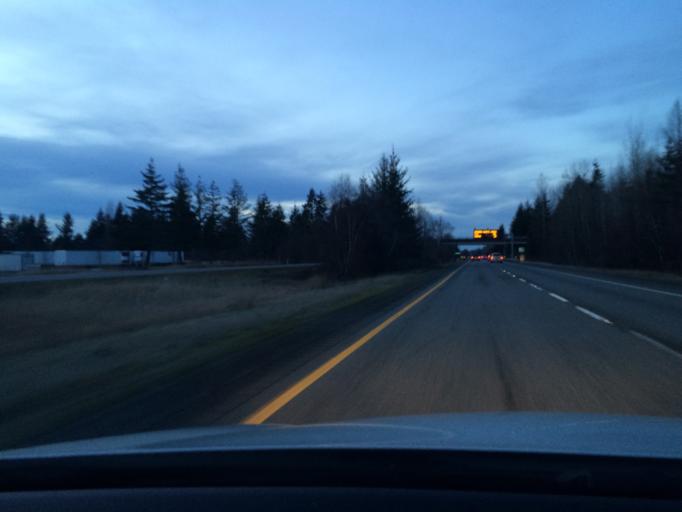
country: US
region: Washington
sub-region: Whatcom County
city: Birch Bay
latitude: 48.9479
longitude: -122.6813
